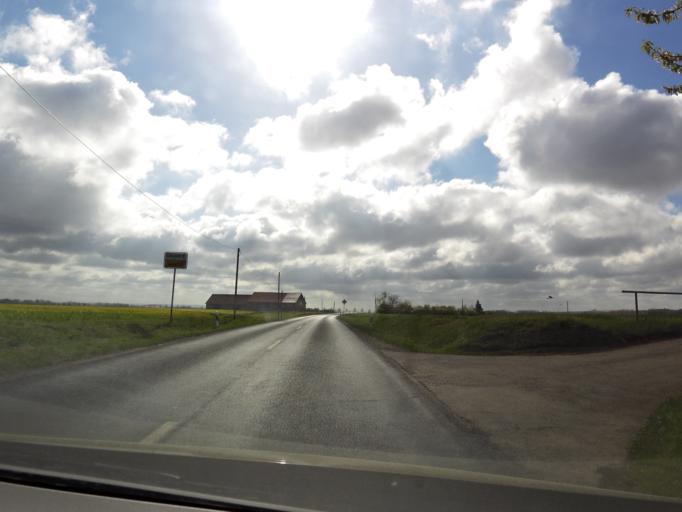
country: DE
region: Thuringia
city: Seebergen
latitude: 50.9189
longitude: 10.8033
